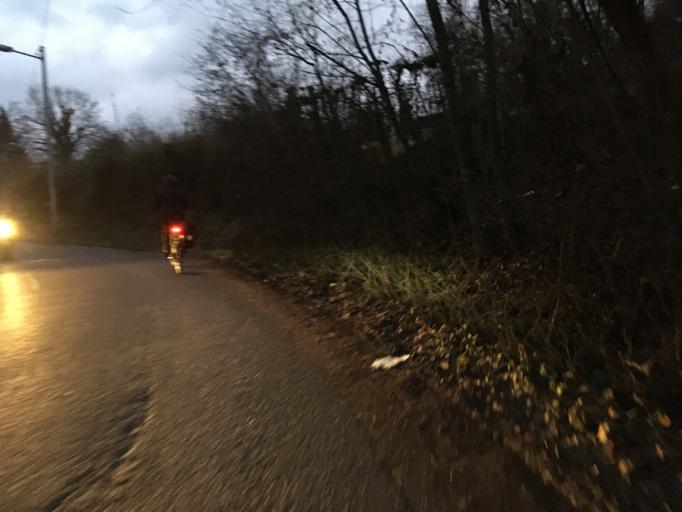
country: DE
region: Baden-Wuerttemberg
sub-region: Regierungsbezirk Stuttgart
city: Kornwestheim
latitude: 48.8381
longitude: 9.1978
